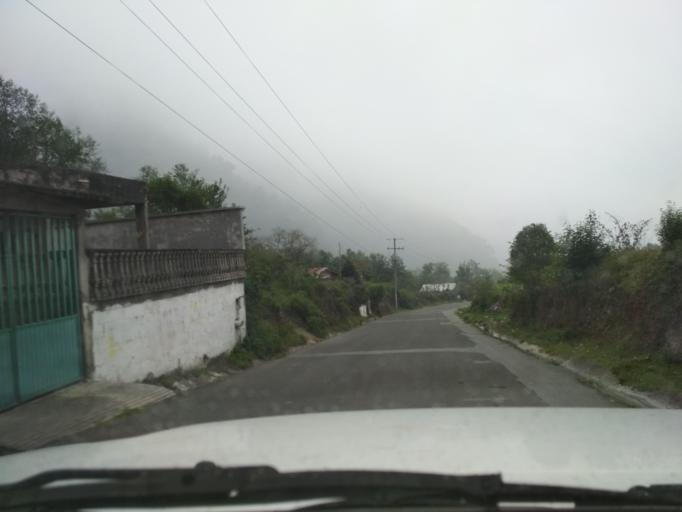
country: MX
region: Veracruz
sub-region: Mariano Escobedo
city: San Isidro el Berro
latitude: 18.9548
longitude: -97.1782
